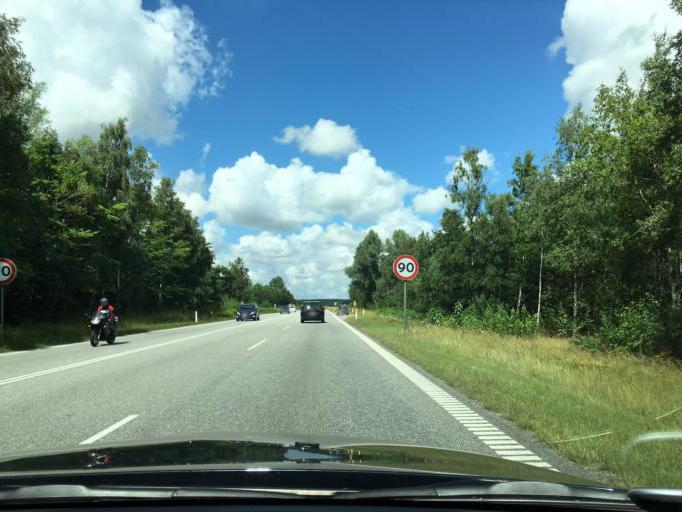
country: DK
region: Capital Region
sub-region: Allerod Kommune
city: Lillerod
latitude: 55.8648
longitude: 12.3169
